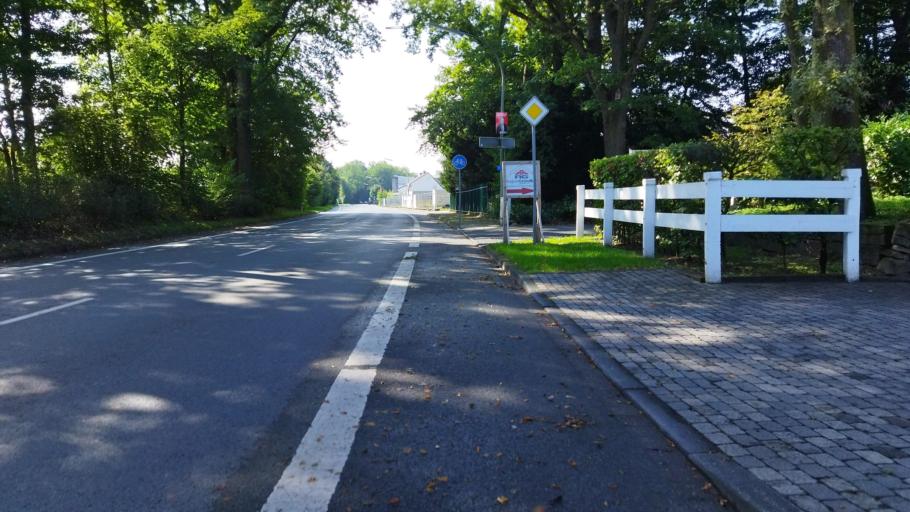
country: DE
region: North Rhine-Westphalia
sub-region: Regierungsbezirk Munster
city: Warendorf
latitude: 51.9754
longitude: 7.9940
